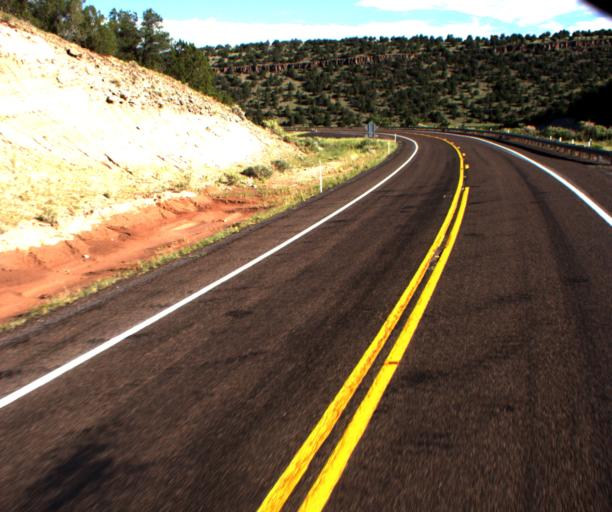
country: US
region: Arizona
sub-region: Apache County
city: Eagar
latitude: 34.0893
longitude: -109.2023
